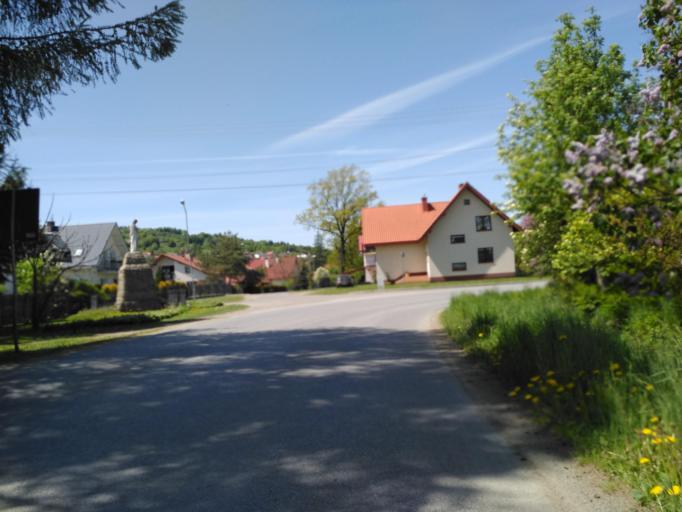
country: PL
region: Subcarpathian Voivodeship
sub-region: Powiat krosnienski
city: Dukla
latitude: 49.5517
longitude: 21.6905
